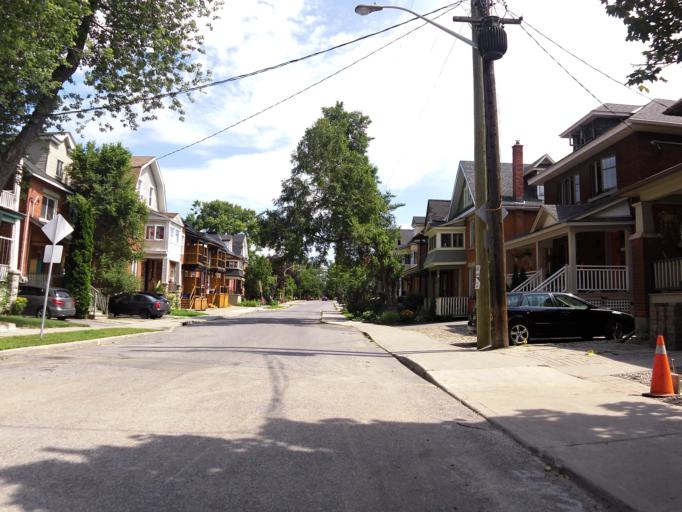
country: CA
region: Ontario
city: Ottawa
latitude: 45.4073
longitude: -75.7012
